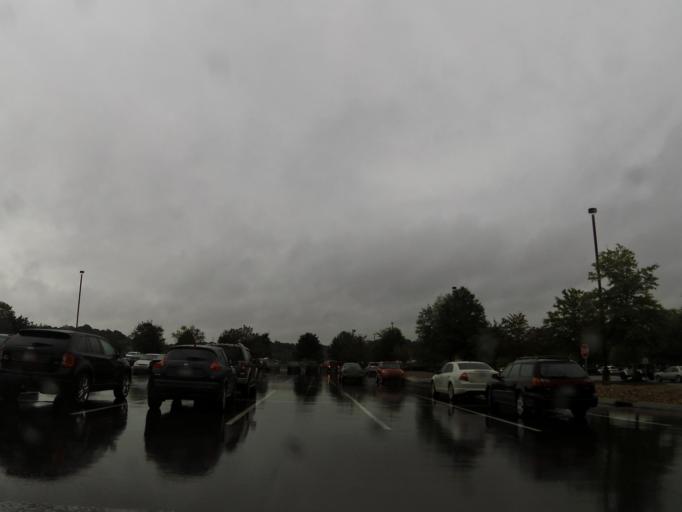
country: US
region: Tennessee
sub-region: Blount County
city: Eagleton Village
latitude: 35.8089
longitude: -83.9490
